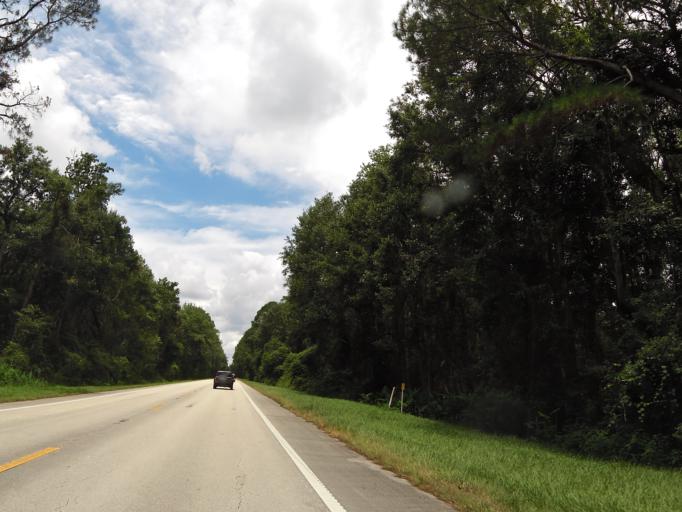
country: US
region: Florida
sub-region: Saint Johns County
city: Saint Augustine Shores
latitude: 29.7270
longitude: -81.4075
